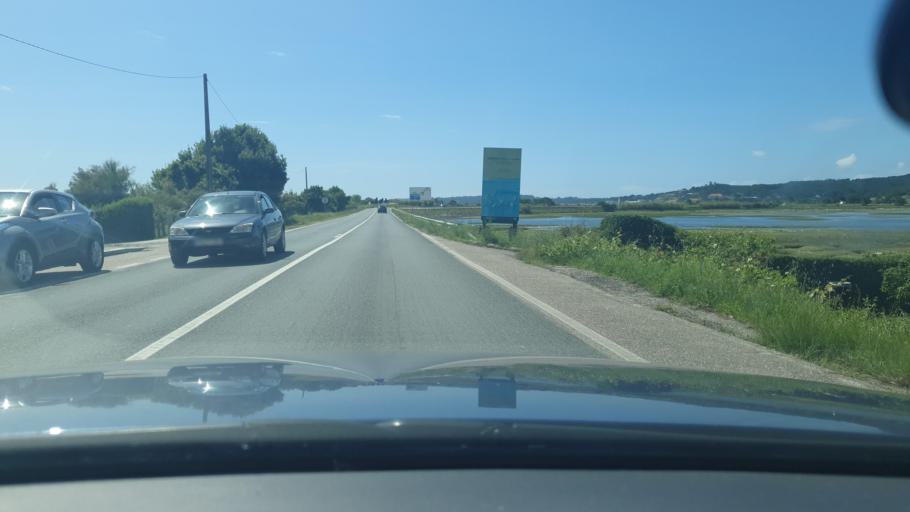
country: ES
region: Galicia
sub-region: Provincia de Pontevedra
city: O Grove
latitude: 42.4471
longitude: -8.8657
